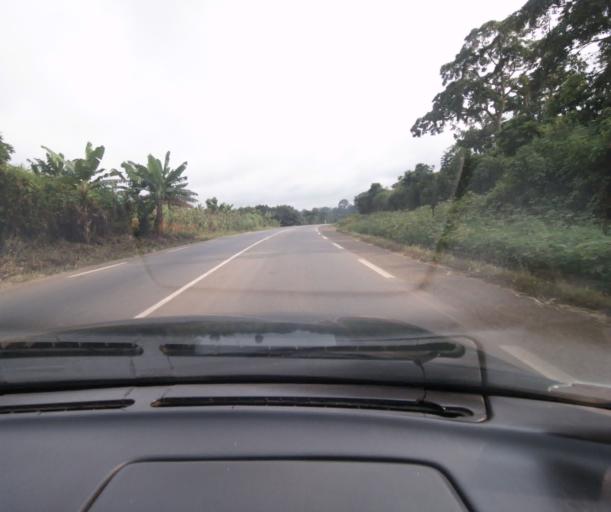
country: CM
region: Centre
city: Obala
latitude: 4.0979
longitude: 11.5376
